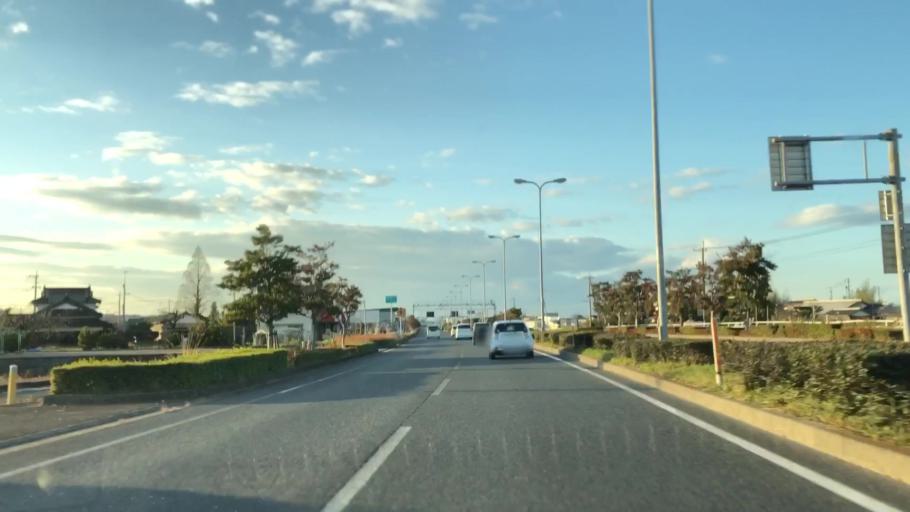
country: JP
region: Fukuoka
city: Nakatsu
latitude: 33.5442
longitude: 131.2863
